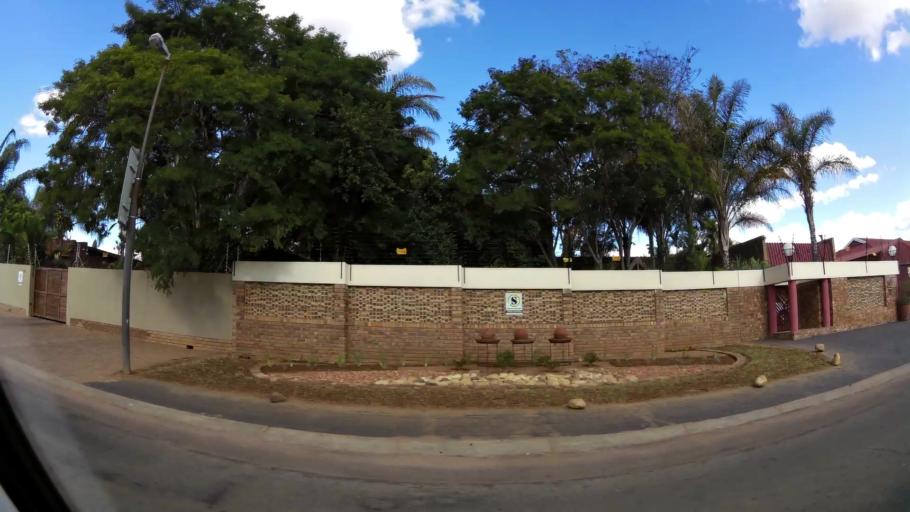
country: ZA
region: Limpopo
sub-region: Capricorn District Municipality
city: Polokwane
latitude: -23.8958
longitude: 29.4752
